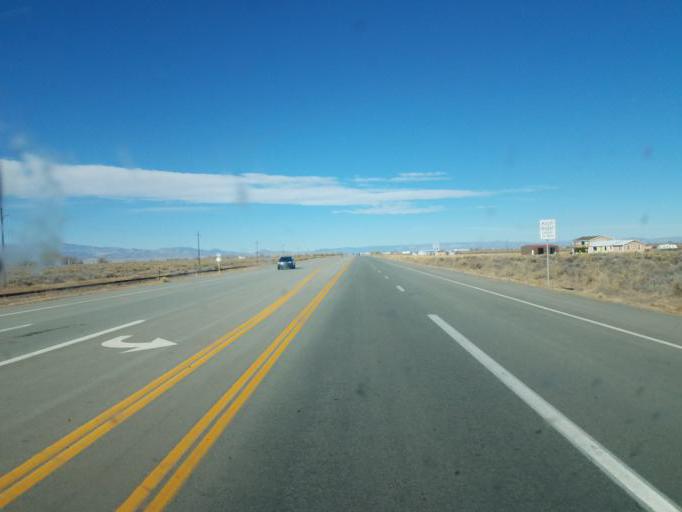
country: US
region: Colorado
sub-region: Alamosa County
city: Alamosa
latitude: 37.5140
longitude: -105.9859
